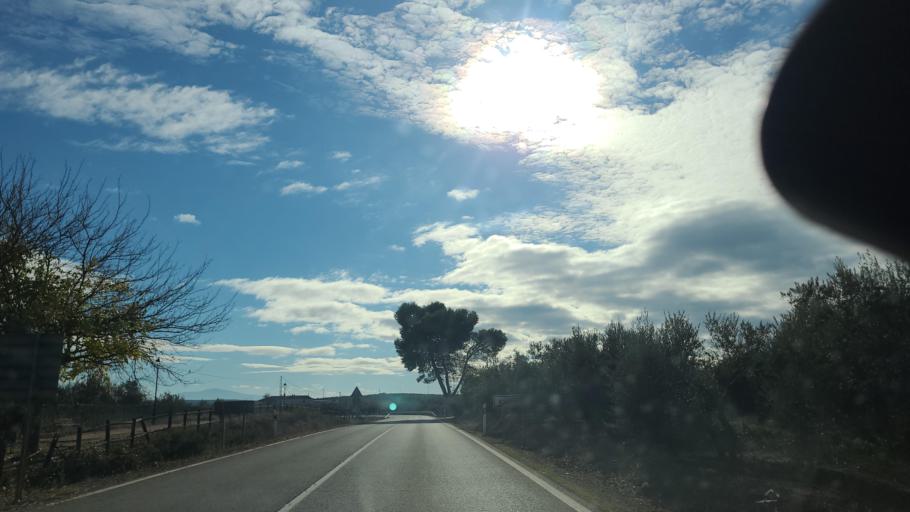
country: ES
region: Andalusia
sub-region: Provincia de Jaen
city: Espeluy
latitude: 38.0296
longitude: -3.8632
